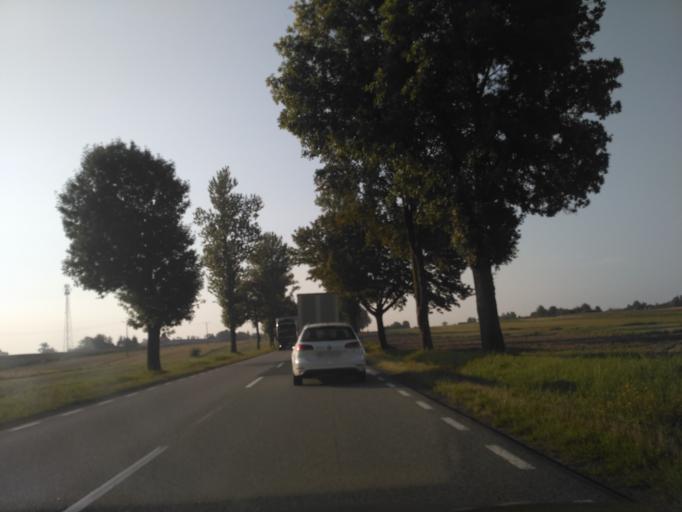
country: PL
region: Lublin Voivodeship
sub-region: Powiat krasnicki
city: Szastarka
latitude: 50.8379
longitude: 22.3013
